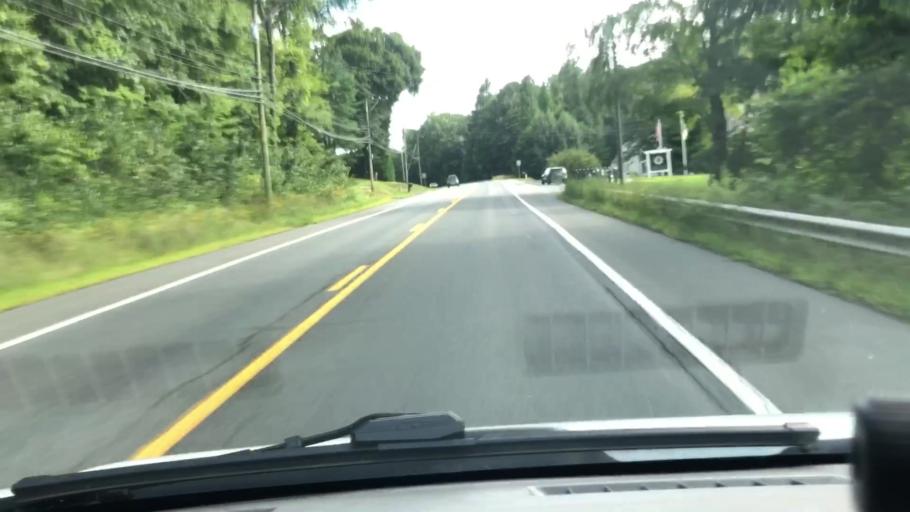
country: US
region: Massachusetts
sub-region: Franklin County
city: Shelburne Falls
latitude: 42.5963
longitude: -72.7282
